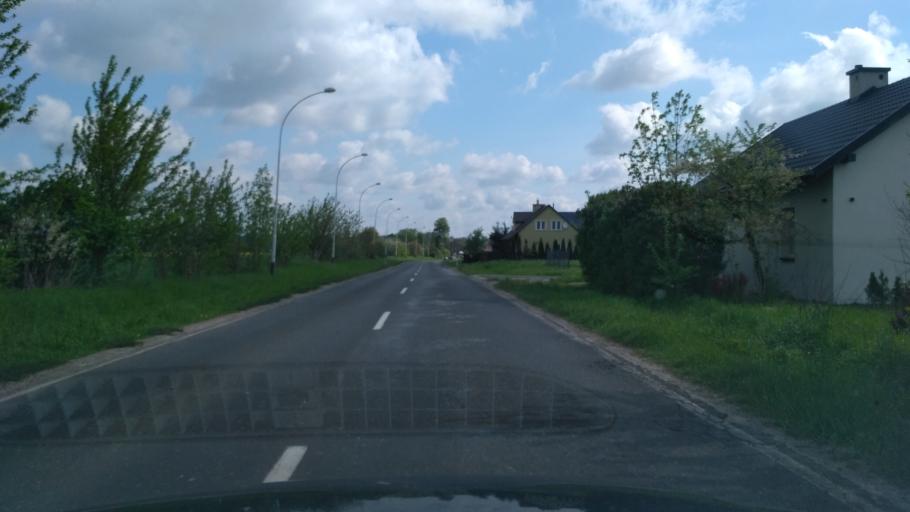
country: PL
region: Subcarpathian Voivodeship
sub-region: Powiat przeworski
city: Przeworsk
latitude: 50.0437
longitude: 22.4801
